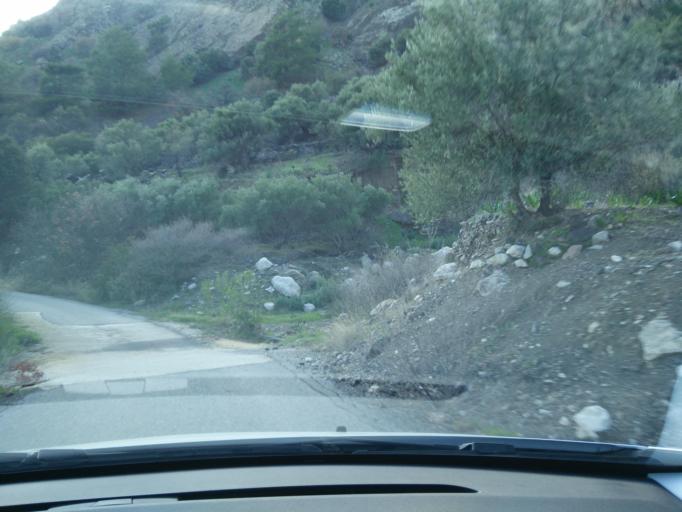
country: GR
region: Crete
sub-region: Nomos Lasithiou
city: Gra Liyia
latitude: 35.0379
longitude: 25.5711
